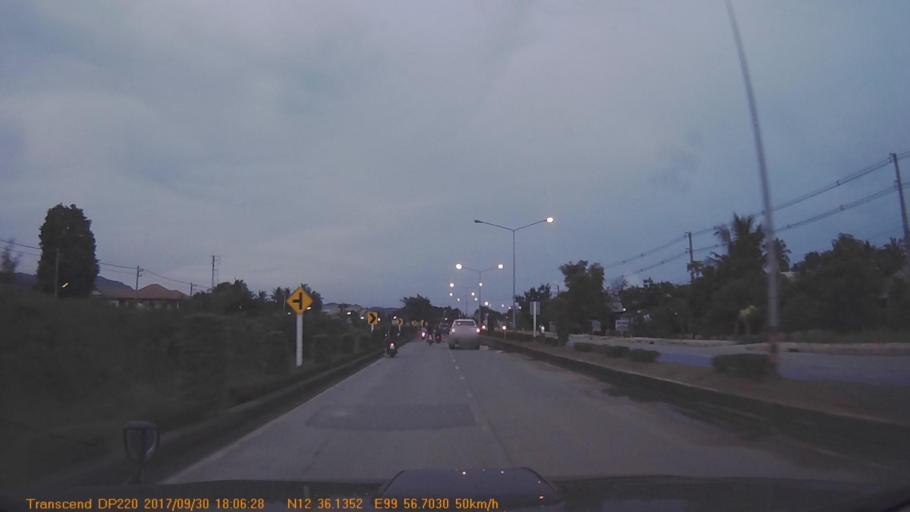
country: TH
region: Prachuap Khiri Khan
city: Hua Hin
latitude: 12.6034
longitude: 99.9449
